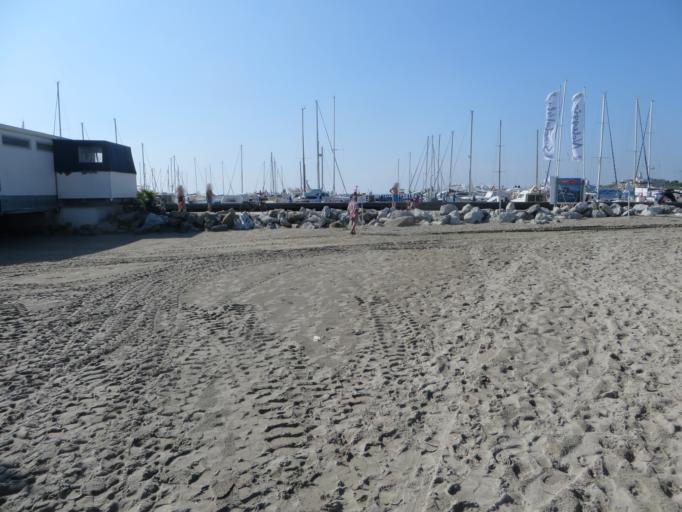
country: IT
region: Emilia-Romagna
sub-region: Provincia di Ravenna
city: Cervia
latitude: 44.2688
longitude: 12.3586
